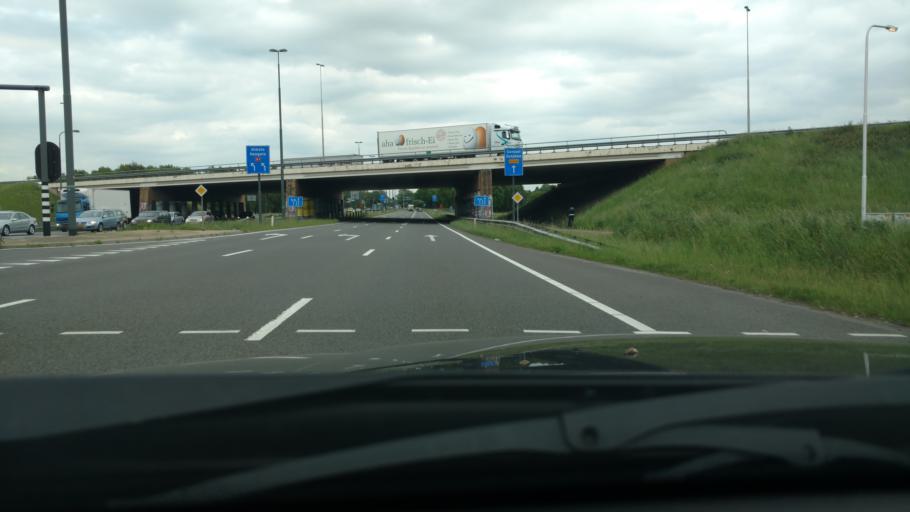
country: NL
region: Gelderland
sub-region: Gemeente Lochem
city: Epse
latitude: 52.2351
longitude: 6.1817
